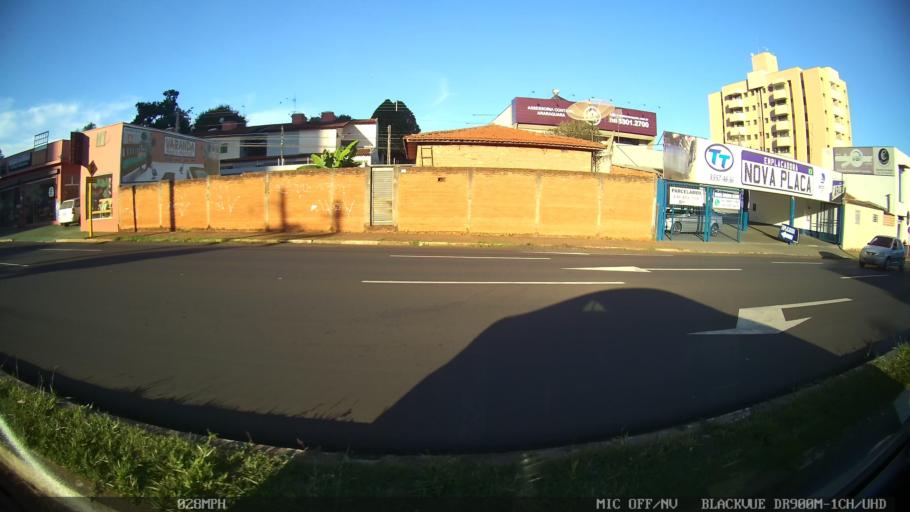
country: BR
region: Sao Paulo
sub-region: Araraquara
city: Araraquara
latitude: -21.7988
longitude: -48.1729
